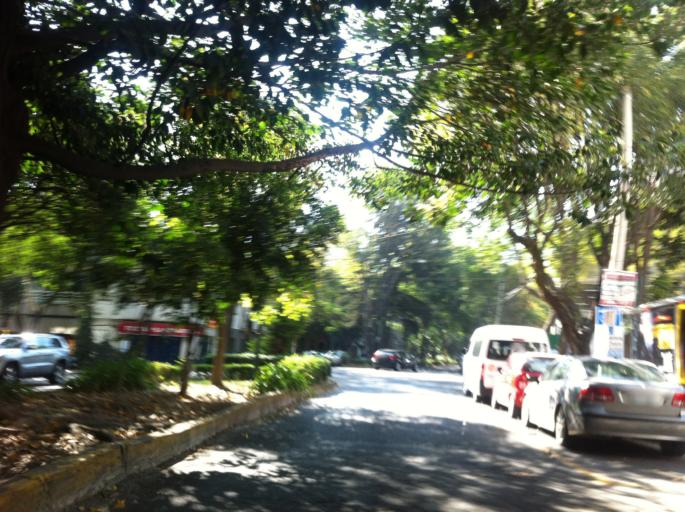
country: MX
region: Mexico City
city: Miguel Hidalgo
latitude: 19.4295
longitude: -99.1874
